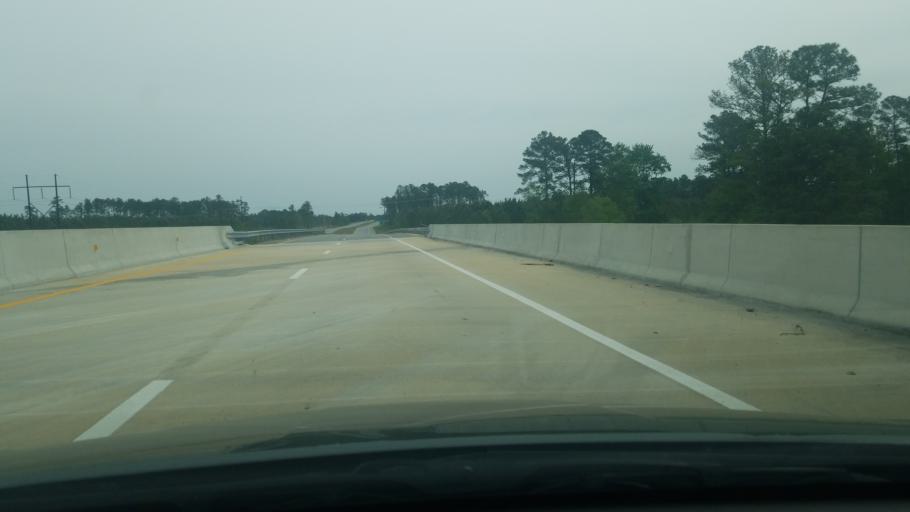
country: US
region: North Carolina
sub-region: Craven County
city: River Bend
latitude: 35.0529
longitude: -77.2129
